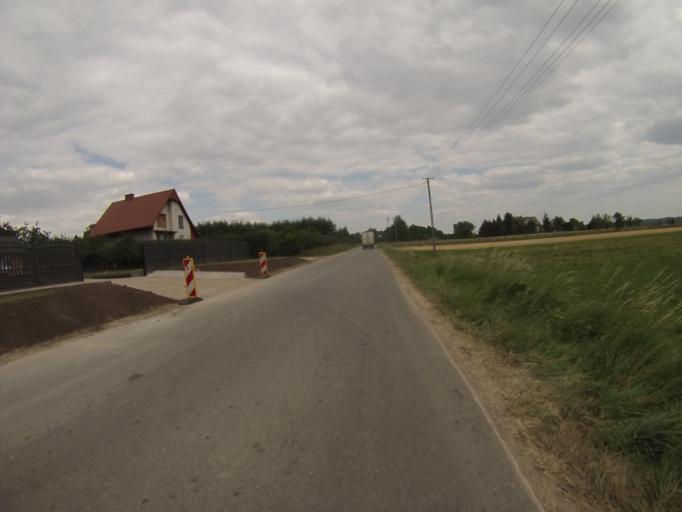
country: PL
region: Swietokrzyskie
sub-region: Powiat staszowski
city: Bogoria
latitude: 50.6870
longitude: 21.2366
